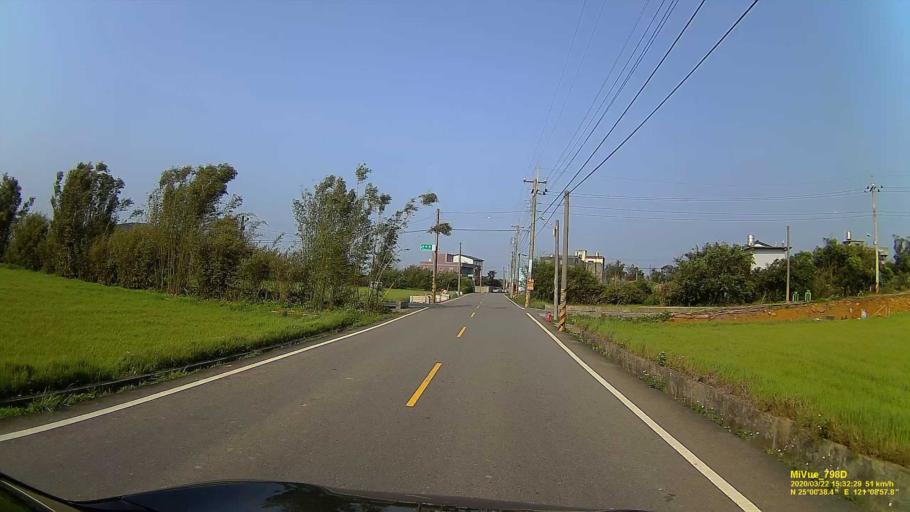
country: TW
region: Taiwan
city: Taoyuan City
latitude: 25.0109
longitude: 121.1497
